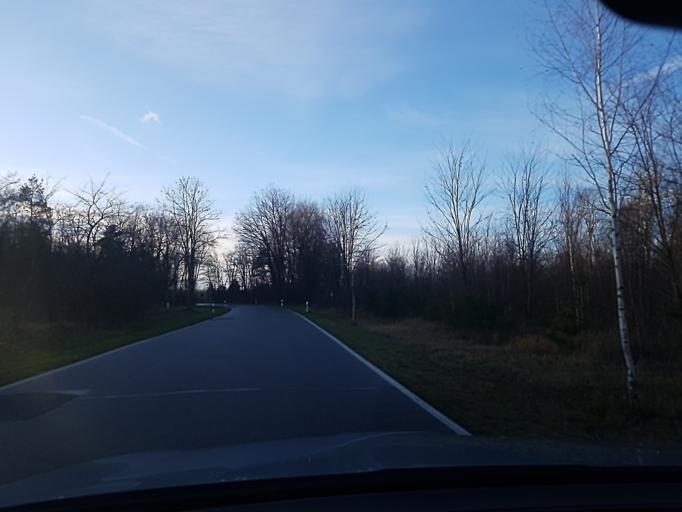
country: DE
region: Brandenburg
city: Trobitz
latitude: 51.5916
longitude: 13.4159
